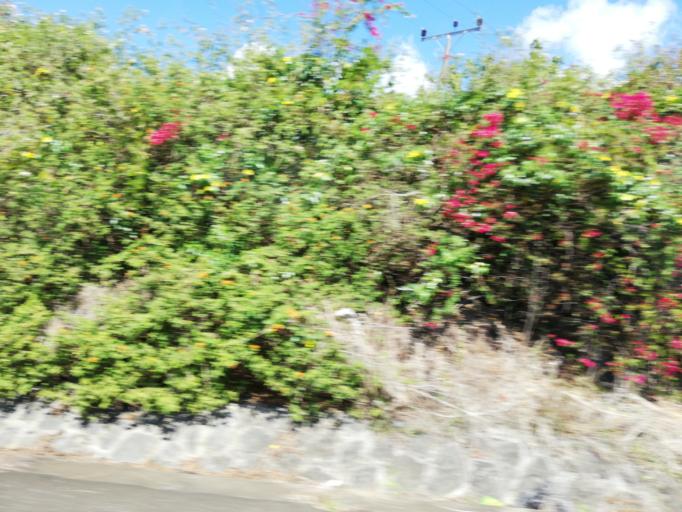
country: MU
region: Riviere du Rempart
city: Goodlands
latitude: -20.0516
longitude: 57.6594
